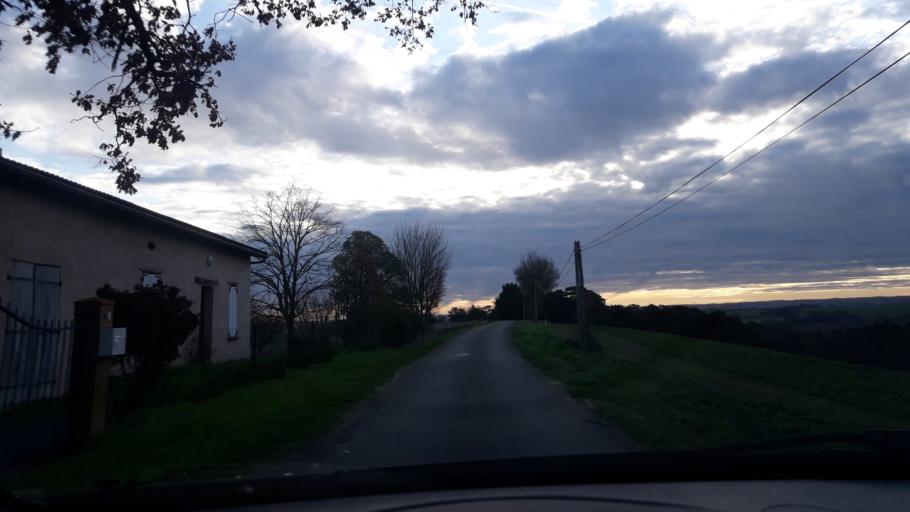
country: FR
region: Midi-Pyrenees
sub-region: Departement du Gers
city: Pujaudran
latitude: 43.6677
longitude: 1.0468
